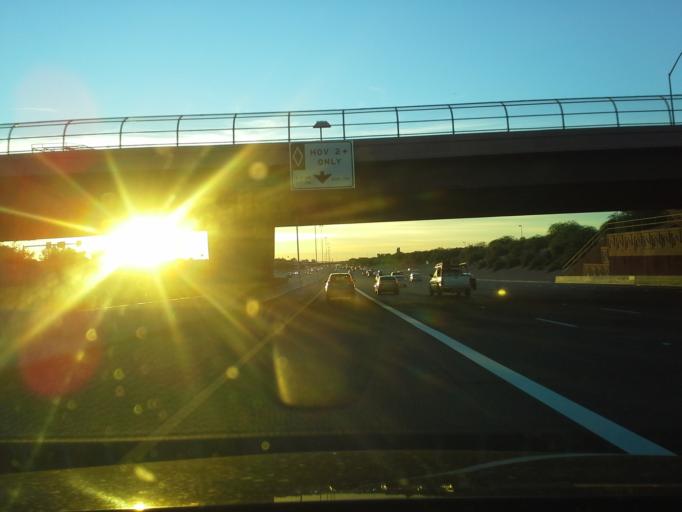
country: US
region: Arizona
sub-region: Pinal County
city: Apache Junction
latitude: 33.3867
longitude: -111.6669
